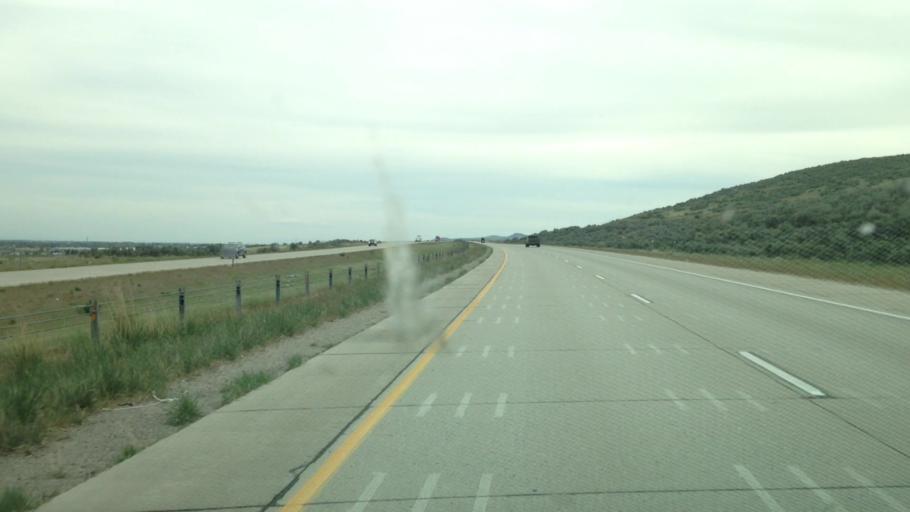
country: US
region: Utah
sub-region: Box Elder County
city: Garland
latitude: 41.7618
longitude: -112.1805
